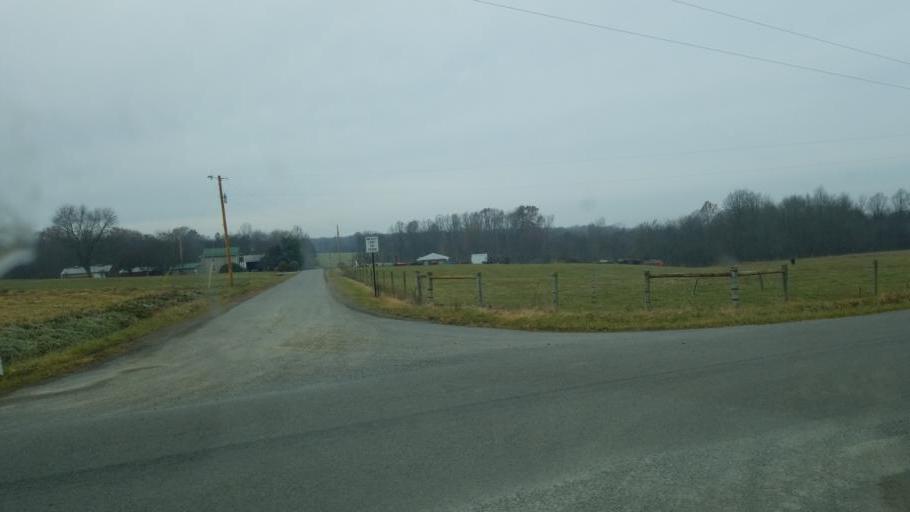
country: US
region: Pennsylvania
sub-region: Crawford County
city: Cochranton
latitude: 41.5078
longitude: -80.1179
